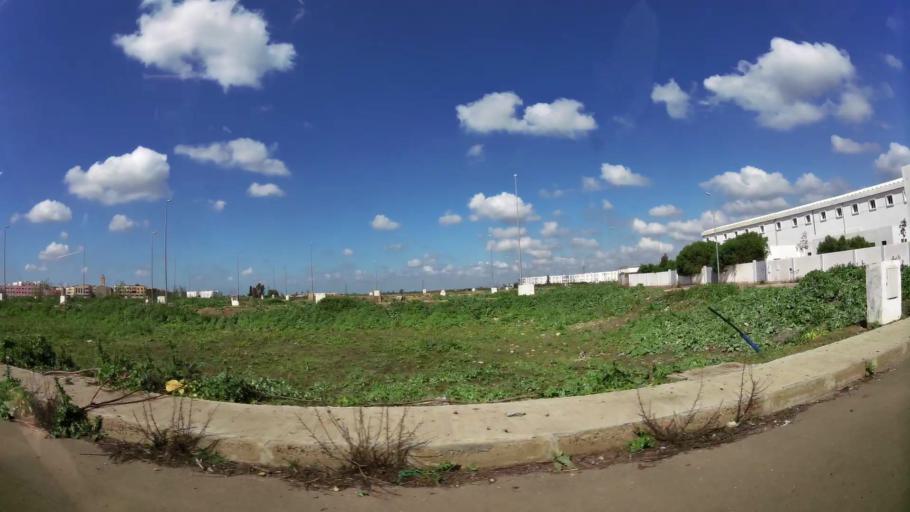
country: MA
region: Grand Casablanca
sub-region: Mediouna
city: Mediouna
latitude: 33.4504
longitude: -7.5066
